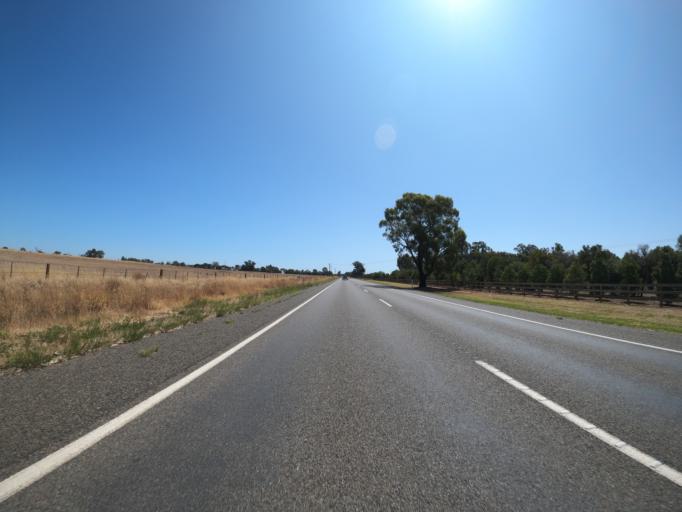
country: AU
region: Victoria
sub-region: Moira
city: Yarrawonga
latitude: -36.0261
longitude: 146.0912
